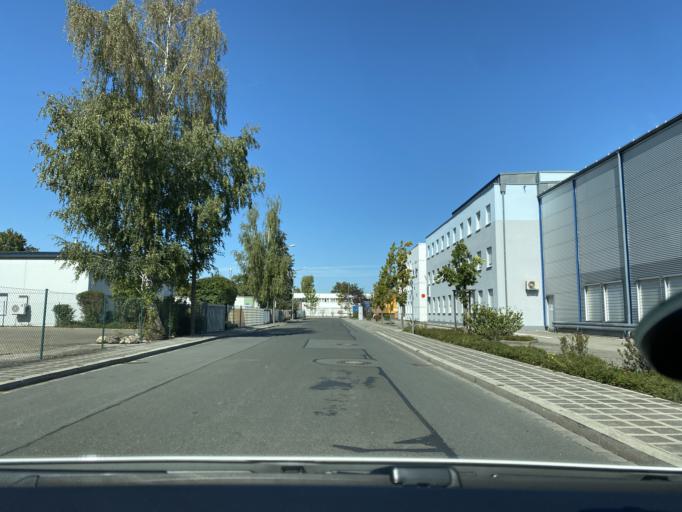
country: DE
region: Bavaria
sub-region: Regierungsbezirk Mittelfranken
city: Furth
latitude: 49.5153
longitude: 11.0008
